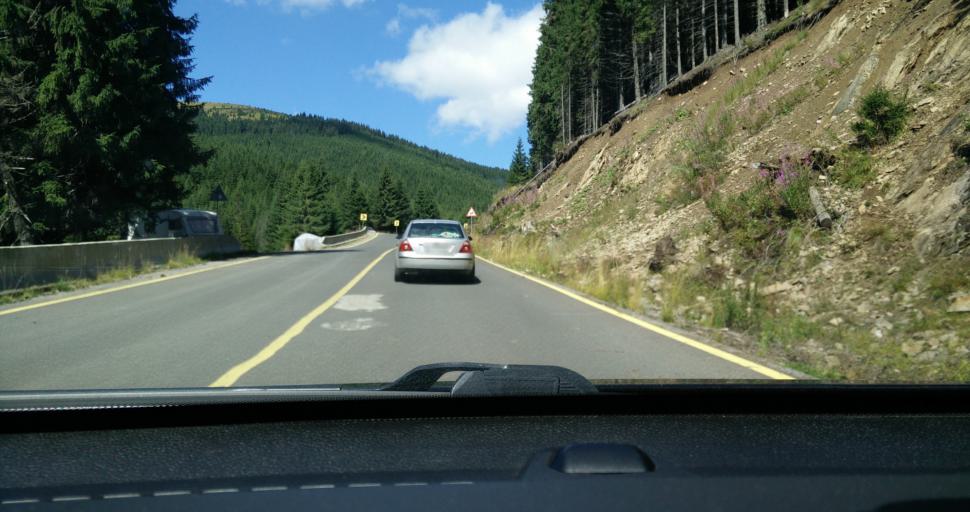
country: RO
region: Hunedoara
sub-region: Oras Petrila
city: Petrila
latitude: 45.4457
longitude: 23.6239
